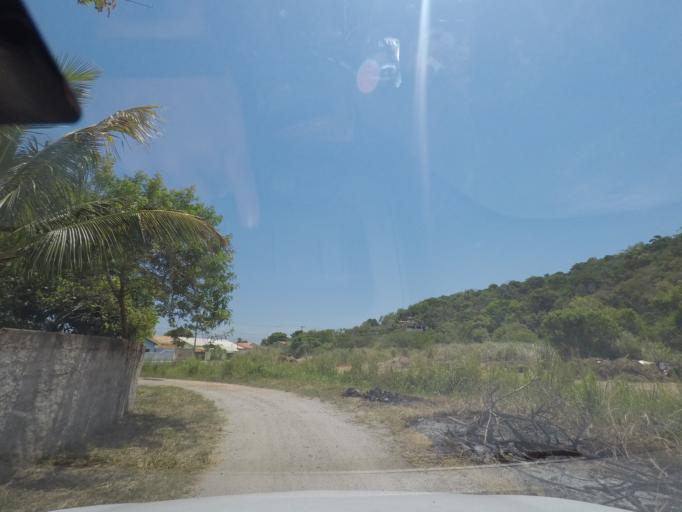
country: BR
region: Rio de Janeiro
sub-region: Niteroi
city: Niteroi
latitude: -22.9562
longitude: -42.9692
